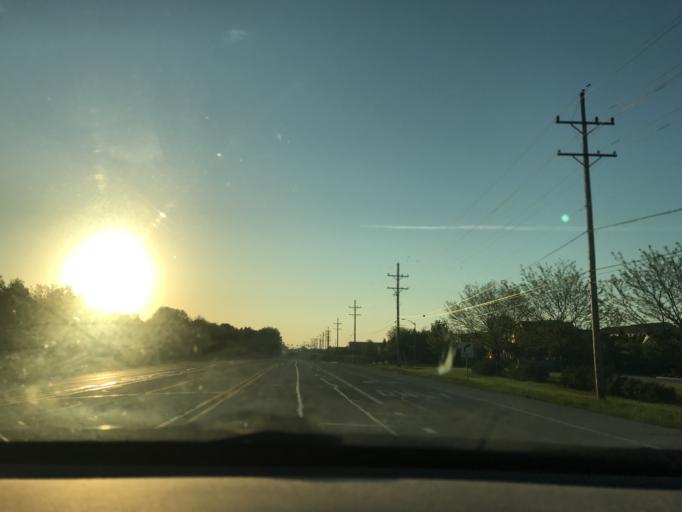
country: US
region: Illinois
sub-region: Kane County
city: South Elgin
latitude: 42.0069
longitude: -88.3457
